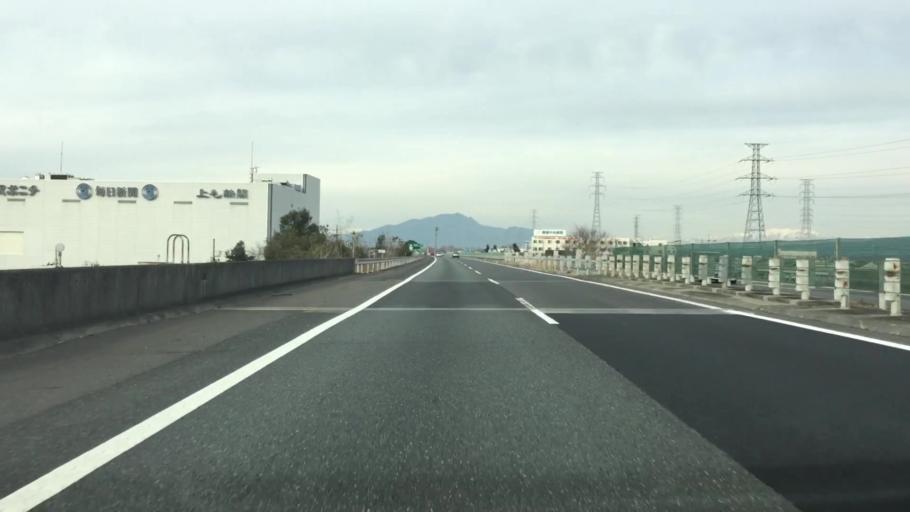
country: JP
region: Gunma
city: Kanekomachi
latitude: 36.4004
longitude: 139.0245
